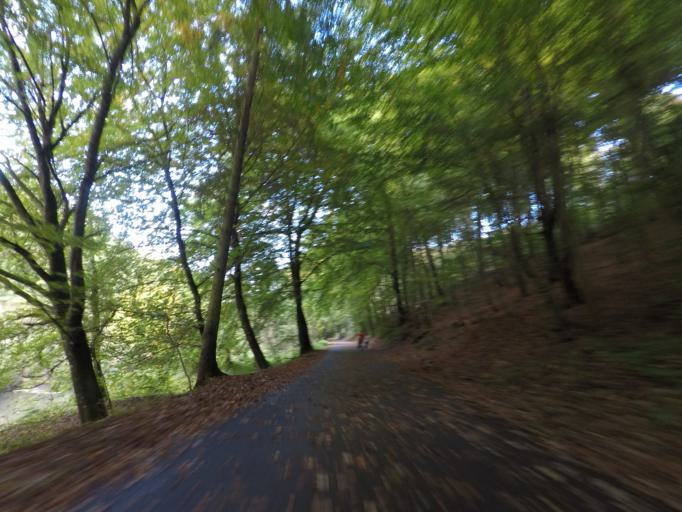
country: LU
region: Luxembourg
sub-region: Canton de Luxembourg
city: Hesperange
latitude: 49.5875
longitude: 6.1528
